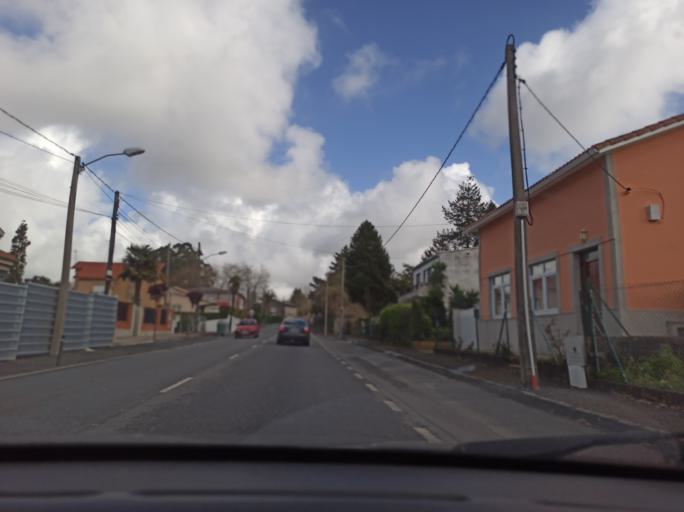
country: ES
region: Galicia
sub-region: Provincia da Coruna
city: Oleiros
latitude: 43.3330
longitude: -8.3100
